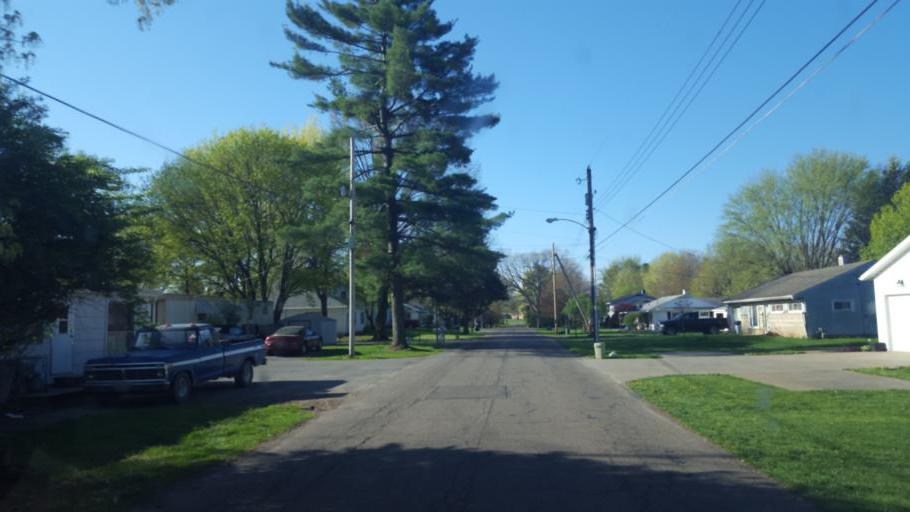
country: US
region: Ohio
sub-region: Morrow County
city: Mount Gilead
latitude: 40.5532
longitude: -82.8504
